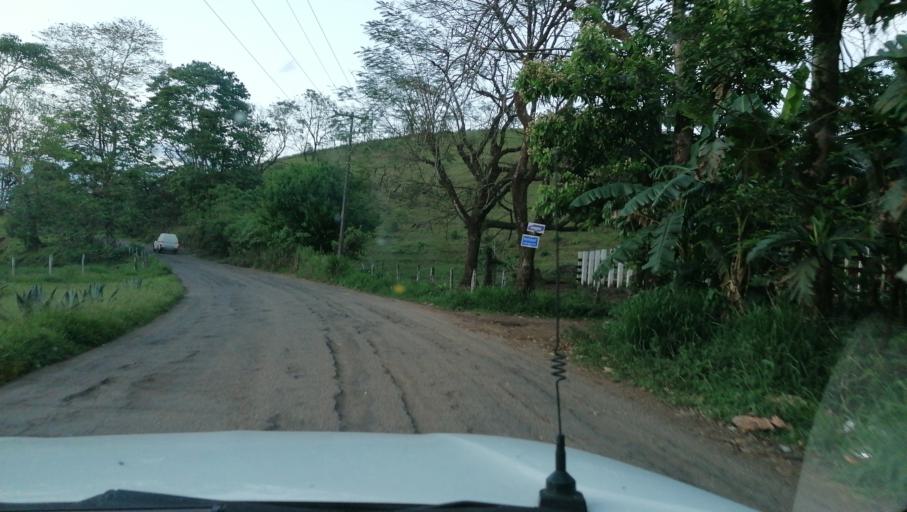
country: MX
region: Chiapas
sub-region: Ostuacan
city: Nuevo Juan del Grijalva
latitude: 17.4300
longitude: -93.3517
